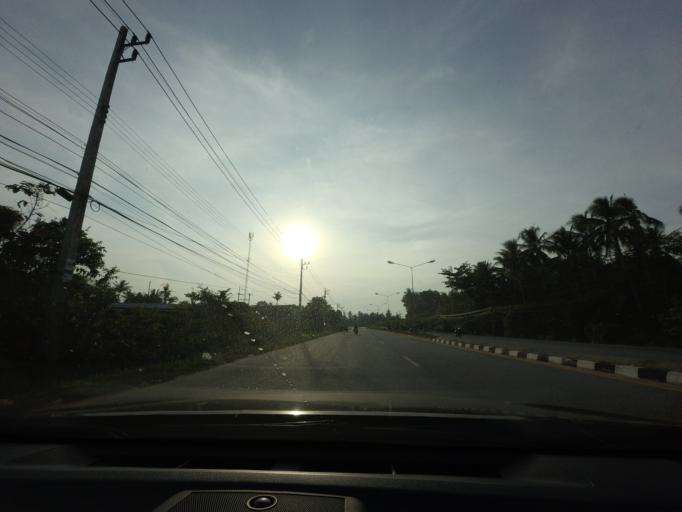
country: TH
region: Narathiwat
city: Narathiwat
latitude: 6.4165
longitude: 101.8488
